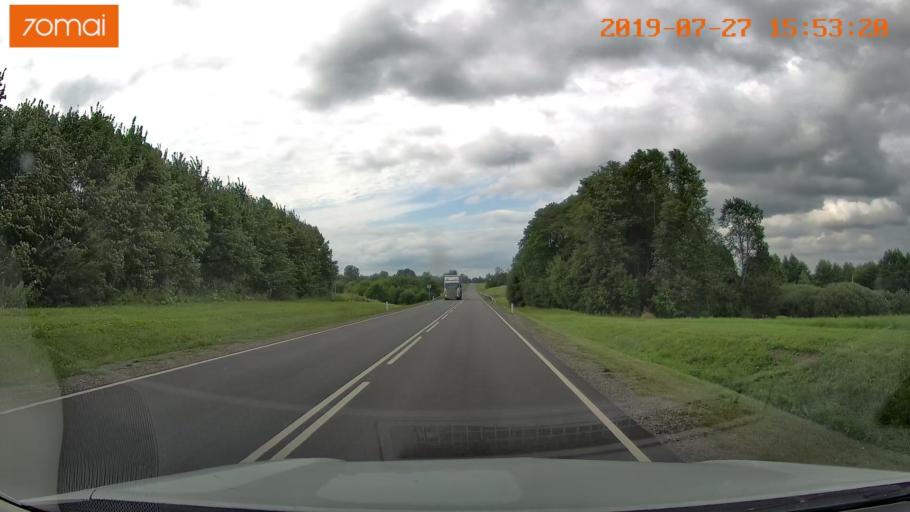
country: RU
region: Kaliningrad
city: Chernyakhovsk
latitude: 54.6031
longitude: 21.9557
